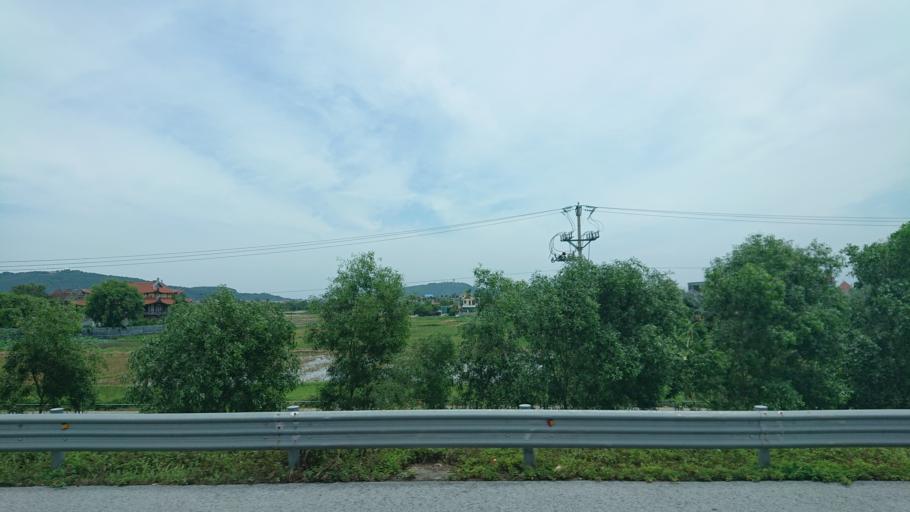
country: VN
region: Hai Phong
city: Nui Doi
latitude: 20.7702
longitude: 106.6243
